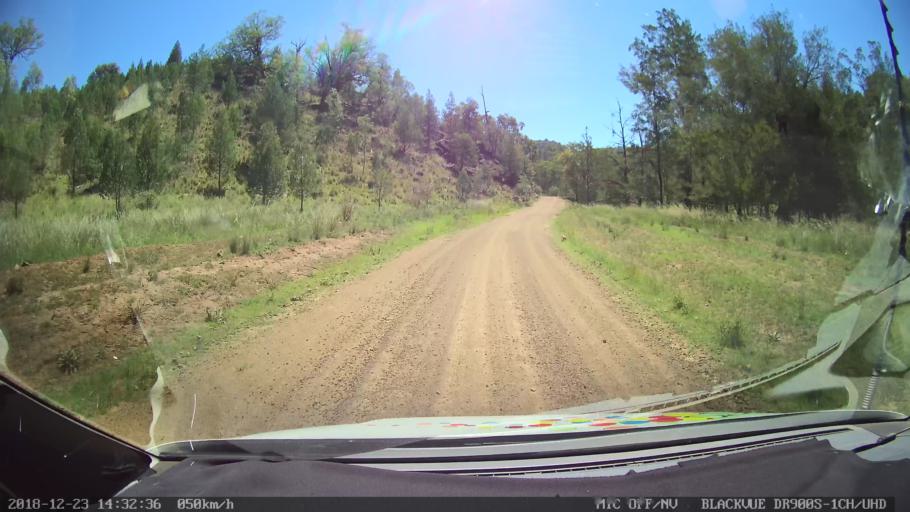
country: AU
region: New South Wales
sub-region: Tamworth Municipality
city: Manilla
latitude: -30.6044
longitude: 150.9175
